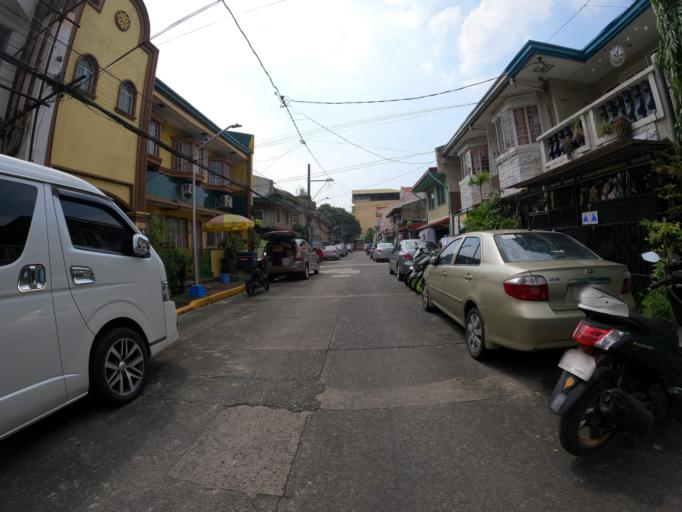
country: PH
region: Metro Manila
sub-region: San Juan
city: San Juan
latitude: 14.5907
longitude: 121.0185
